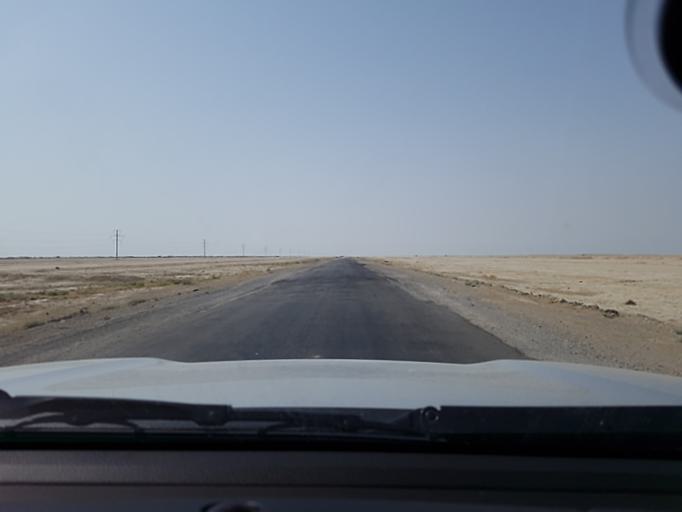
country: TM
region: Balkan
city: Gumdag
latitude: 38.8467
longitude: 54.5956
